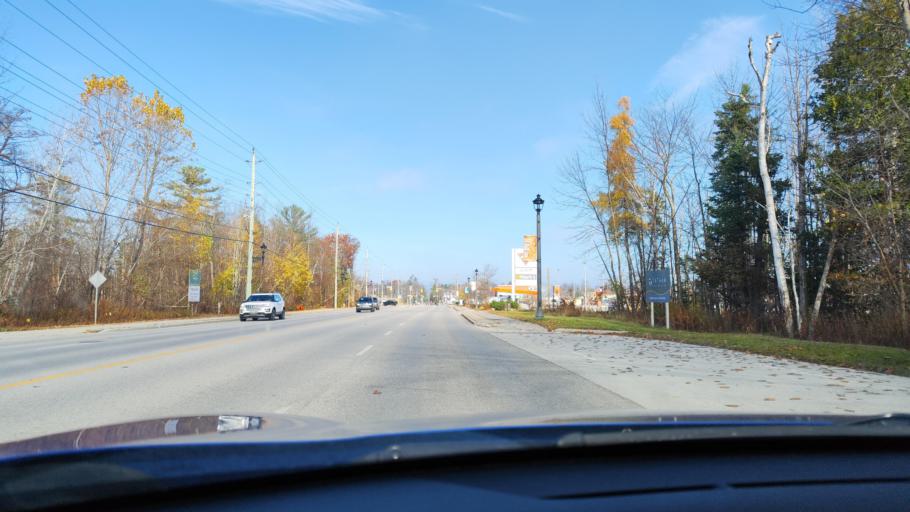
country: CA
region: Ontario
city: Wasaga Beach
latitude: 44.4703
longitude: -80.0753
